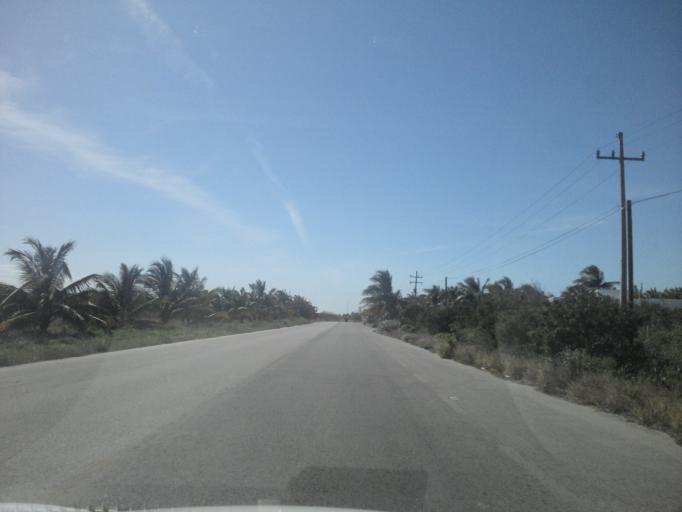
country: MX
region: Yucatan
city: Telchac Puerto
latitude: 21.3314
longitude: -89.3724
